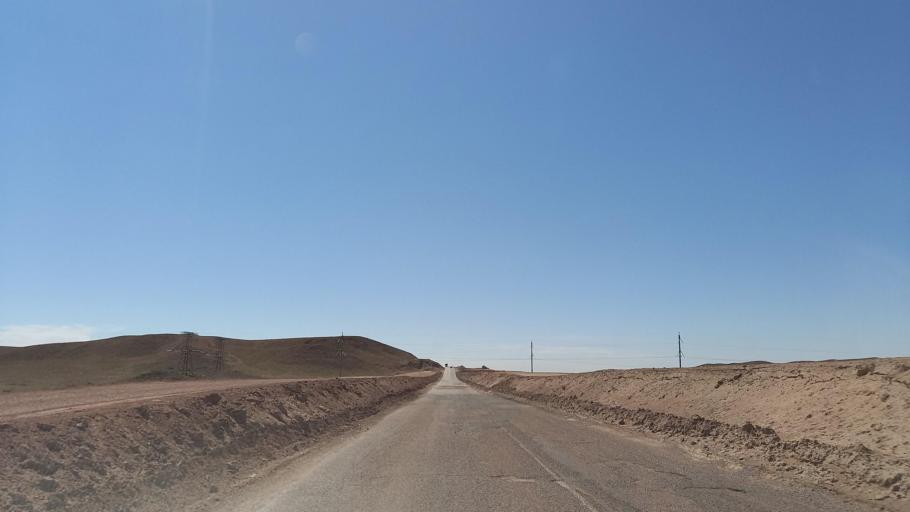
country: KZ
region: Zhambyl
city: Mynaral
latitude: 45.4451
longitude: 73.6069
